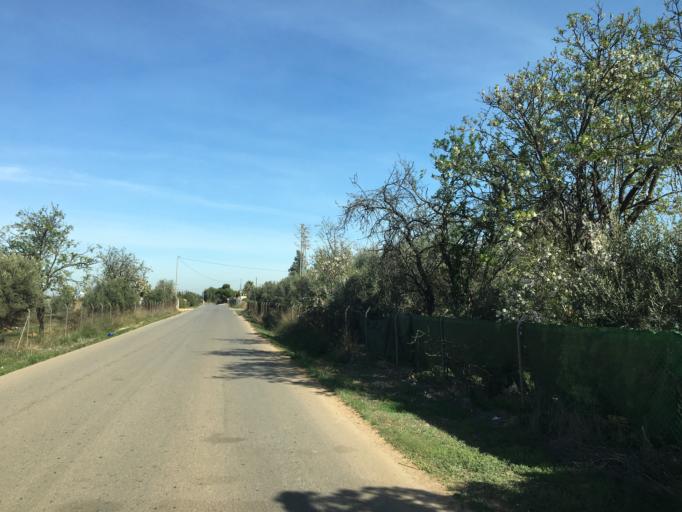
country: ES
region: Murcia
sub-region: Murcia
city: Cartagena
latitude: 37.6522
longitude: -1.0244
